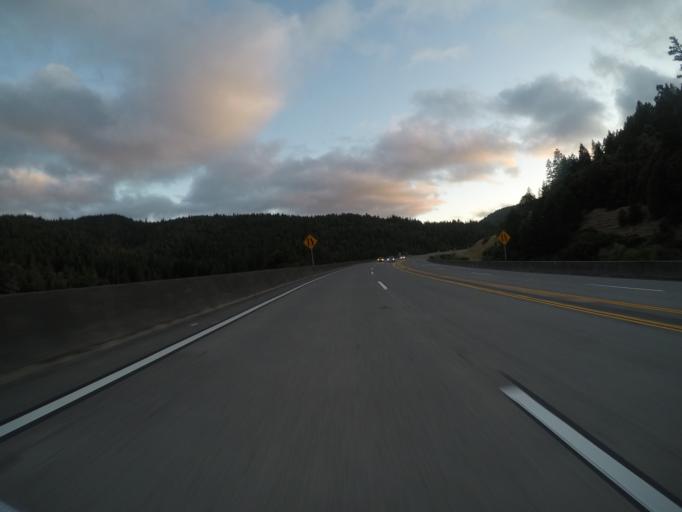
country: US
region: California
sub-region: Humboldt County
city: Redway
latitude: 40.0332
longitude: -123.7771
